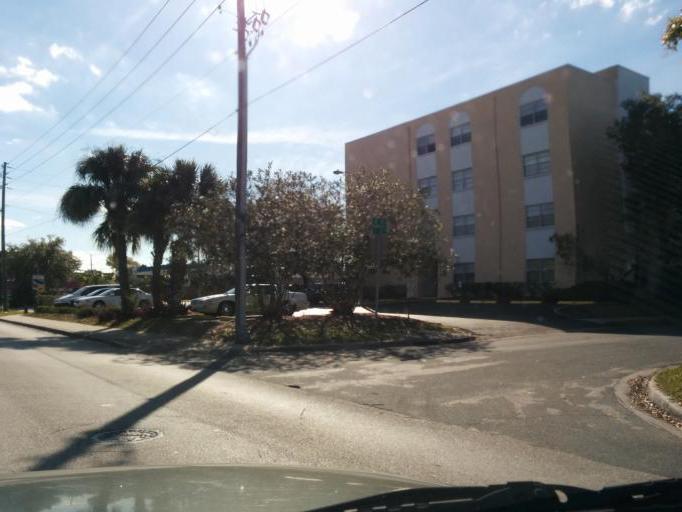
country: US
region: Florida
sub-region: Pinellas County
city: Lealman
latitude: 27.8095
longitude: -82.6345
